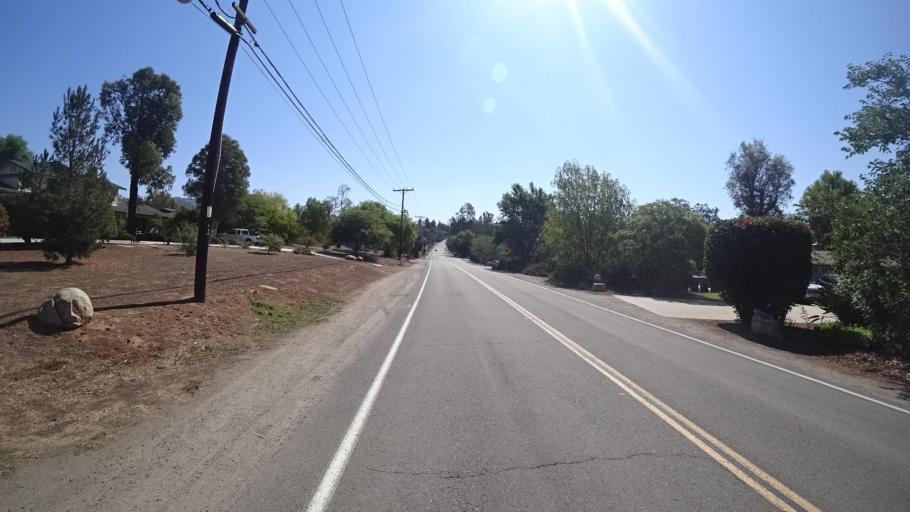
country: US
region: California
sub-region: San Diego County
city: Granite Hills
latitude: 32.7954
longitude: -116.9140
